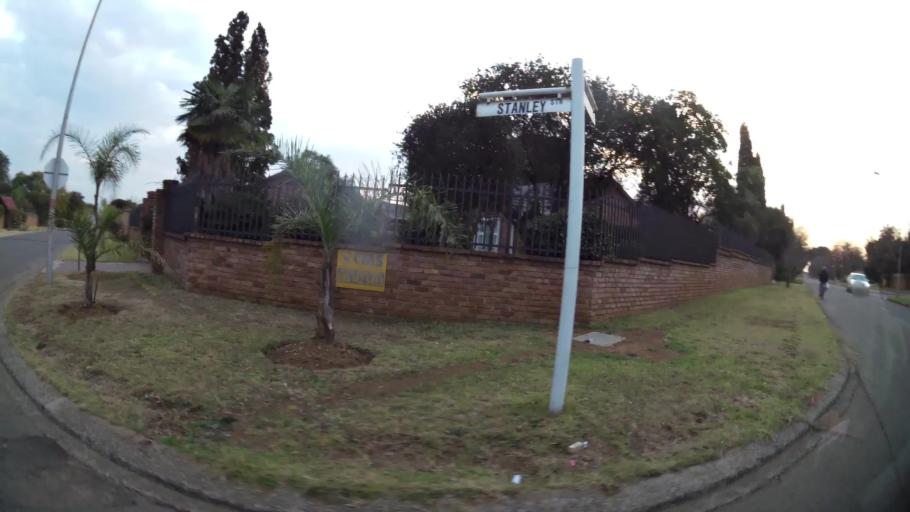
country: ZA
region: Gauteng
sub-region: Ekurhuleni Metropolitan Municipality
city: Benoni
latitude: -26.1714
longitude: 28.3046
